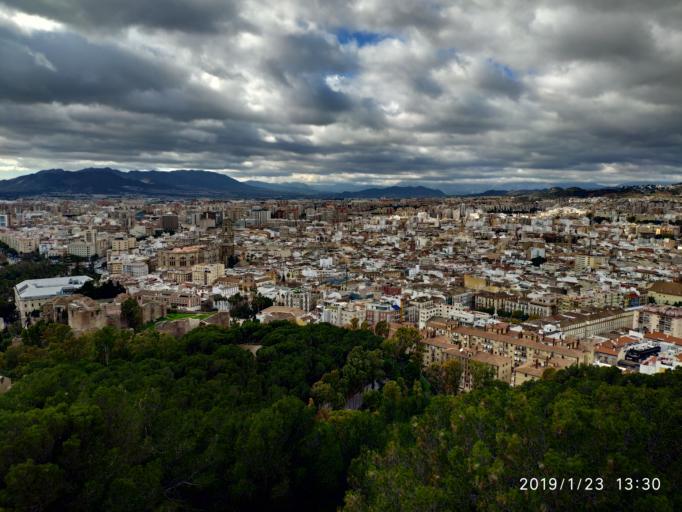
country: ES
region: Andalusia
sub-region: Provincia de Malaga
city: Malaga
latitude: 36.7231
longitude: -4.4128
